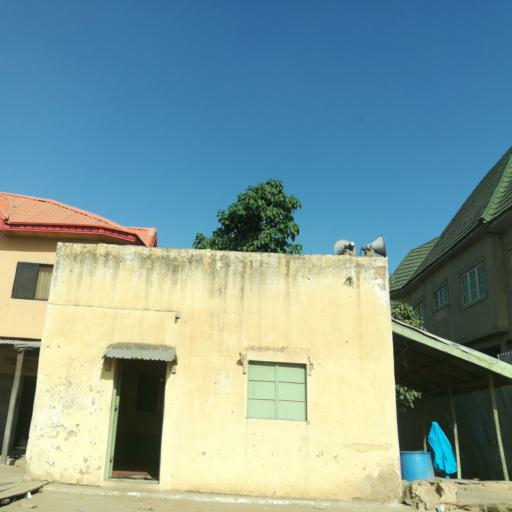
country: NG
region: Kano
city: Kano
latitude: 12.0187
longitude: 8.5040
